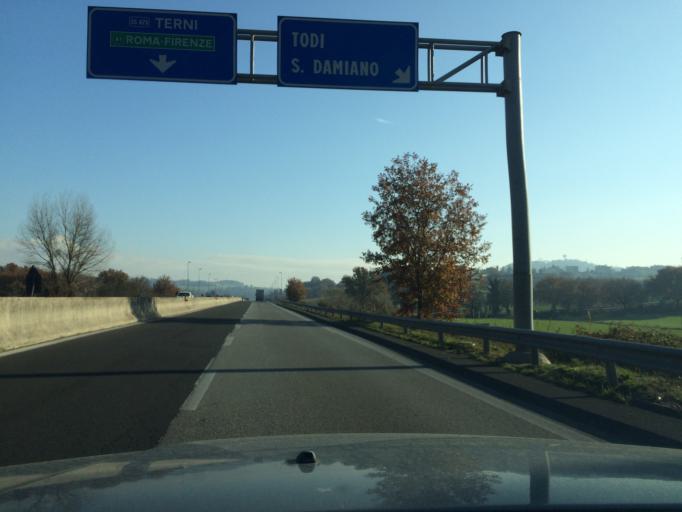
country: IT
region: Umbria
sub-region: Provincia di Perugia
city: Todi
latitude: 42.7884
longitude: 12.4270
